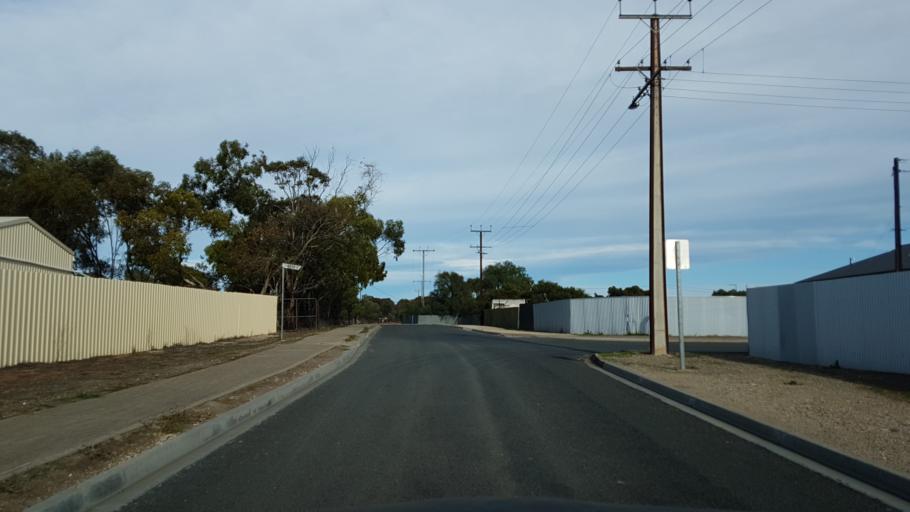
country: AU
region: South Australia
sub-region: Murray Bridge
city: Tailem Bend
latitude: -35.2504
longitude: 139.4541
